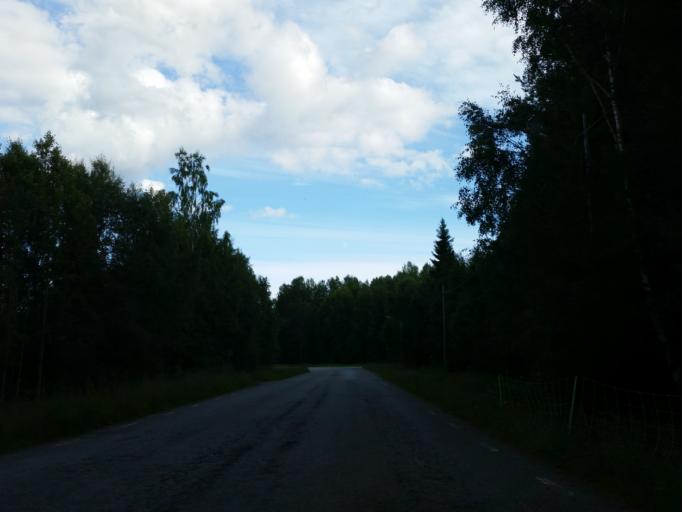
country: SE
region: Vaesterbotten
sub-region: Robertsfors Kommun
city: Robertsfors
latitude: 64.0480
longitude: 20.8510
